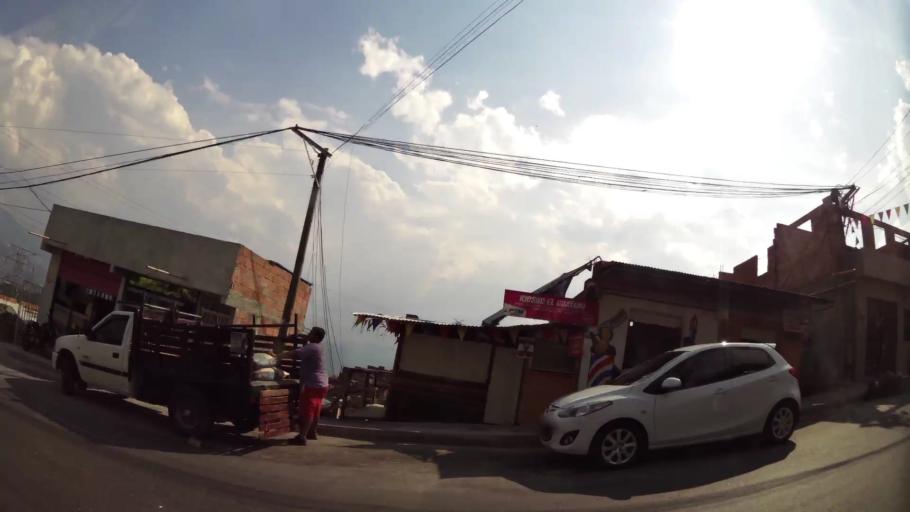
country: CO
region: Antioquia
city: Medellin
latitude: 6.2902
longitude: -75.5919
